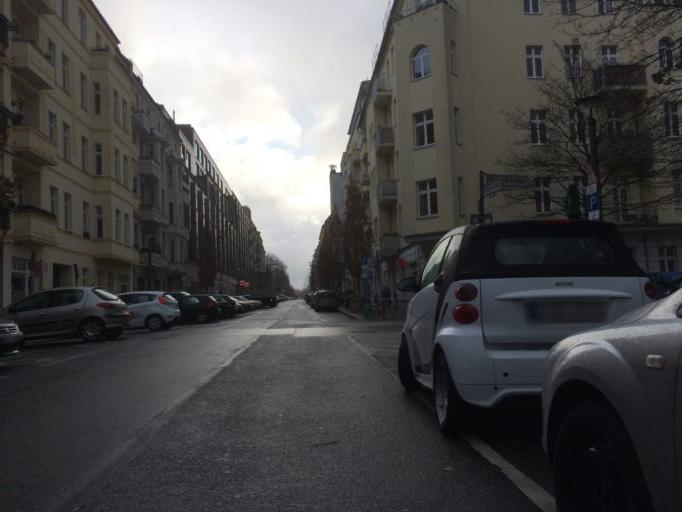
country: DE
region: Berlin
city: Prenzlauer Berg Bezirk
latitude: 52.5337
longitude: 13.4330
